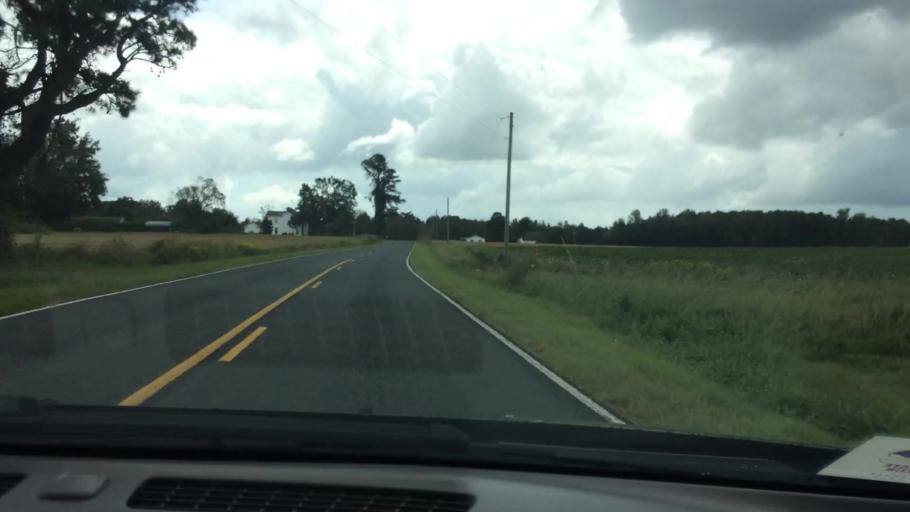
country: US
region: North Carolina
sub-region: Greene County
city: Maury
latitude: 35.4916
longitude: -77.5203
